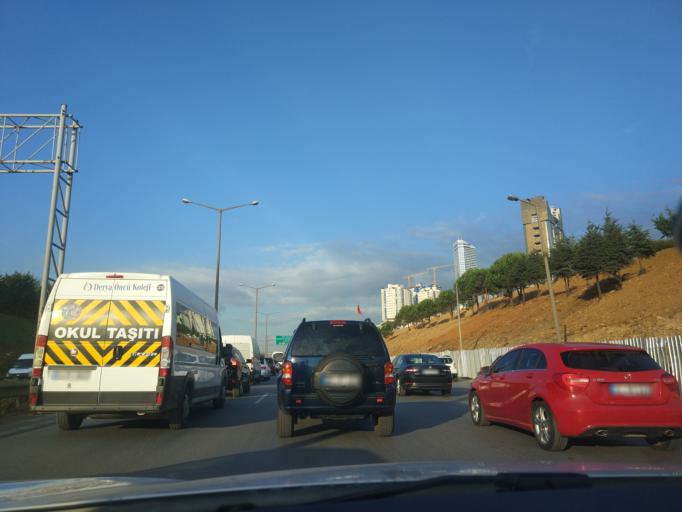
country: TR
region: Istanbul
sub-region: Atasehir
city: Atasehir
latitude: 40.9888
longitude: 29.1096
